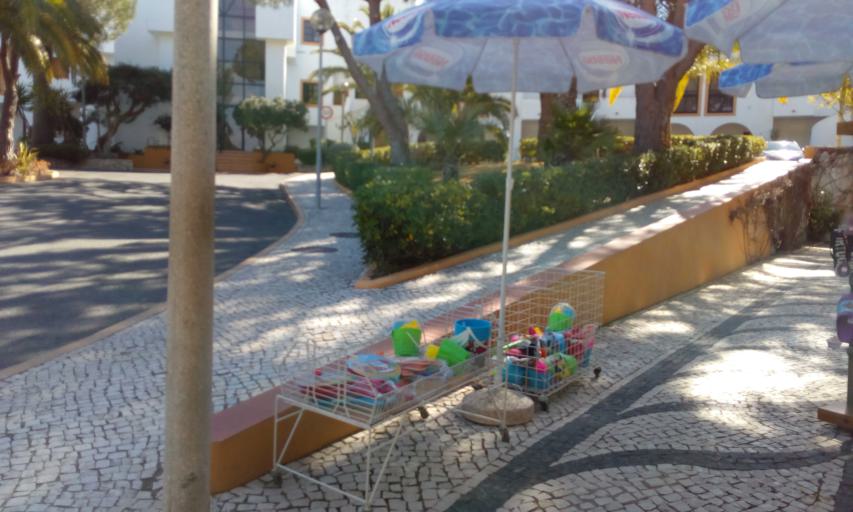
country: PT
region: Faro
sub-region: Albufeira
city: Albufeira
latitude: 37.0900
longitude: -8.2092
